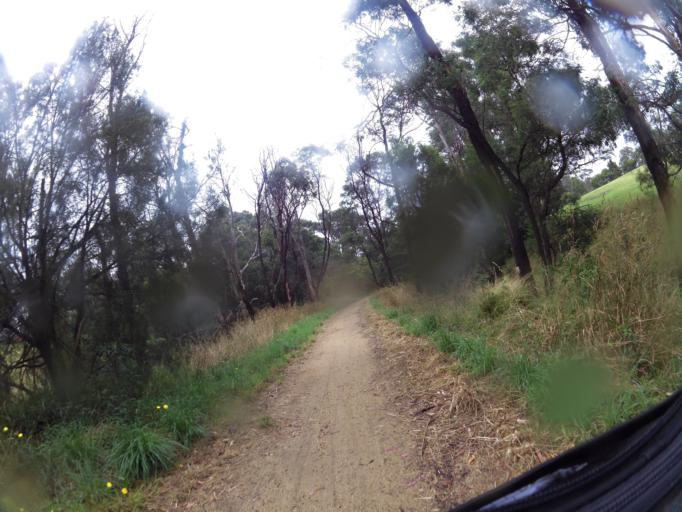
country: AU
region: Victoria
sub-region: East Gippsland
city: Lakes Entrance
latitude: -37.7655
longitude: 147.8206
